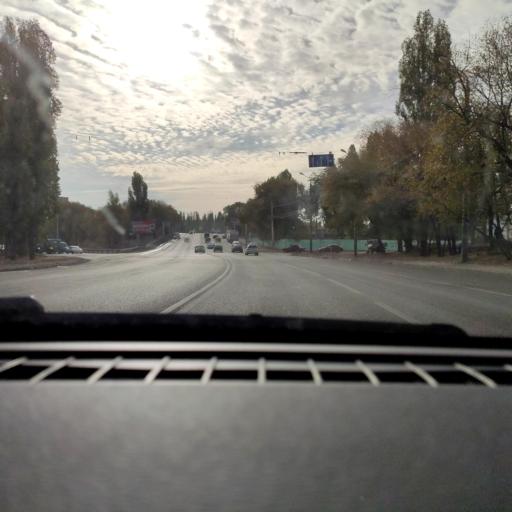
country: RU
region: Voronezj
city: Voronezh
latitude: 51.6246
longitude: 39.2326
